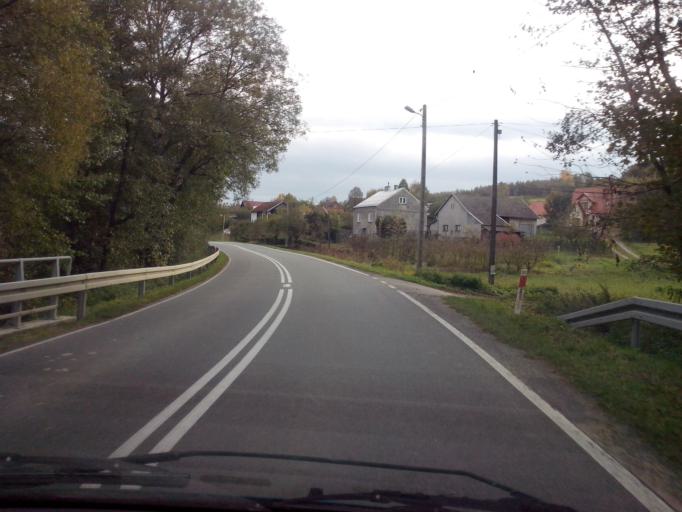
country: PL
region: Subcarpathian Voivodeship
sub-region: Powiat strzyzowski
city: Wisniowa
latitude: 49.8895
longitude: 21.6437
